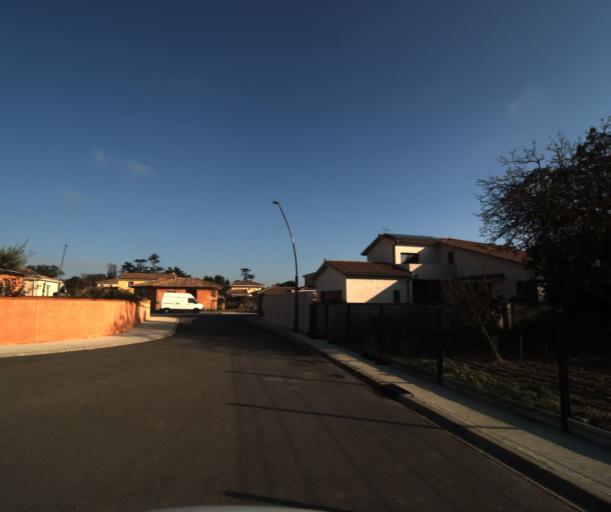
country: FR
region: Midi-Pyrenees
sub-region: Departement de la Haute-Garonne
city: Colomiers
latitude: 43.5926
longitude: 1.3446
